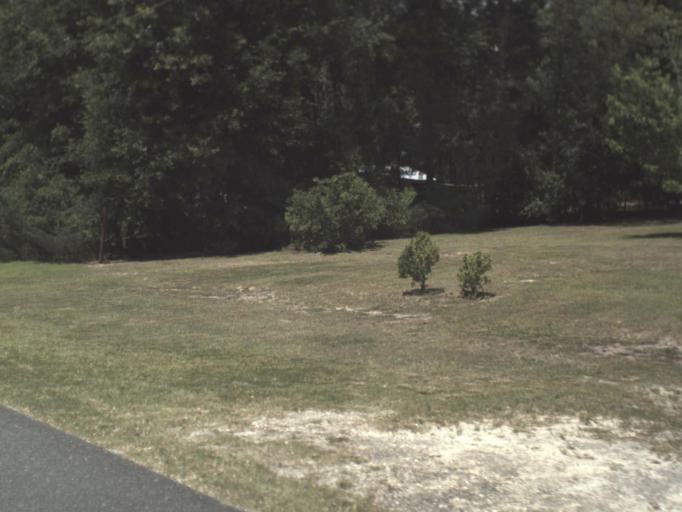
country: US
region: Florida
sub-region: Gilchrist County
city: Trenton
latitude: 29.8128
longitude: -82.8671
